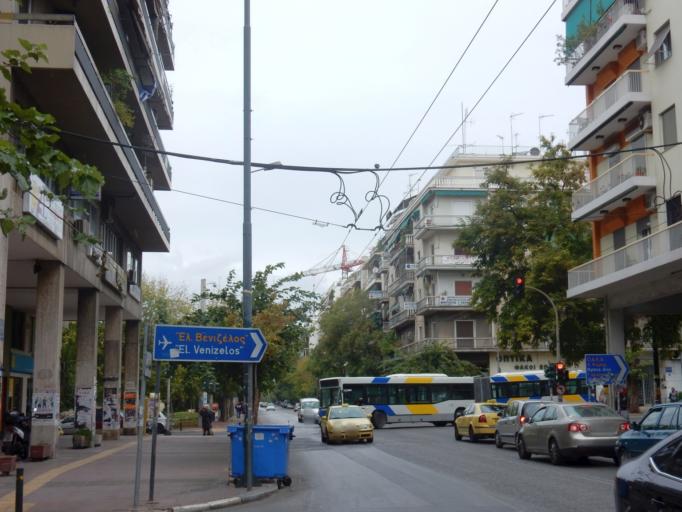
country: GR
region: Attica
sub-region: Nomarchia Athinas
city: Kipseli
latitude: 38.0152
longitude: 23.7353
